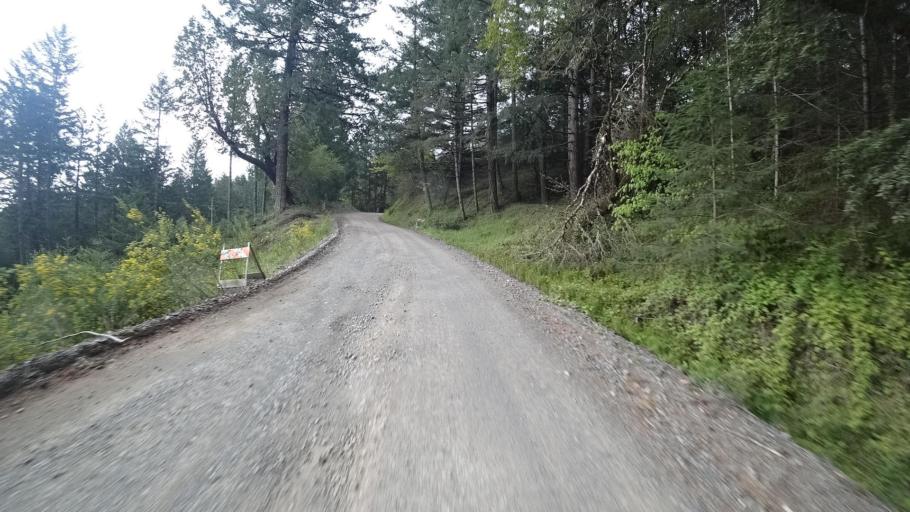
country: US
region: California
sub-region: Humboldt County
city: Redway
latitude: 40.2599
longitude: -123.7679
